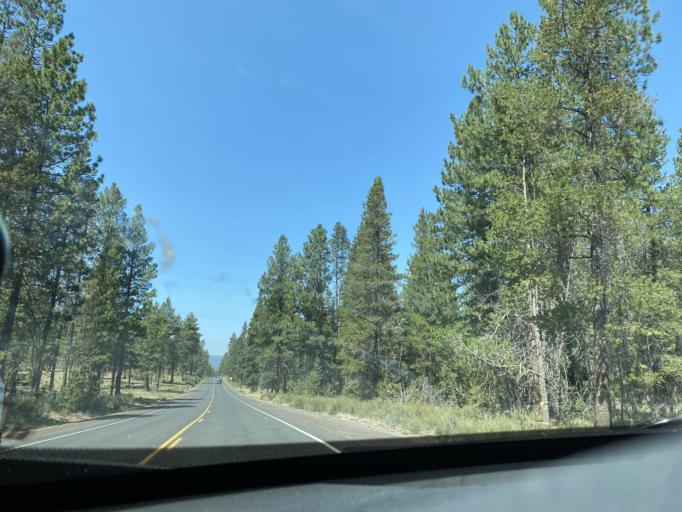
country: US
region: Oregon
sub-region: Deschutes County
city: Sunriver
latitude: 43.8909
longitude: -121.4038
